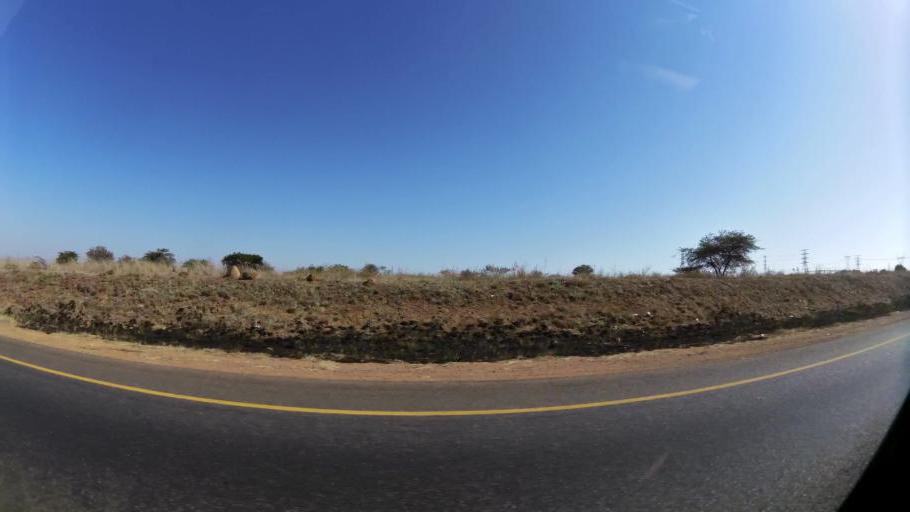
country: ZA
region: Gauteng
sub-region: City of Tshwane Metropolitan Municipality
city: Mabopane
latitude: -25.5665
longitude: 28.1075
